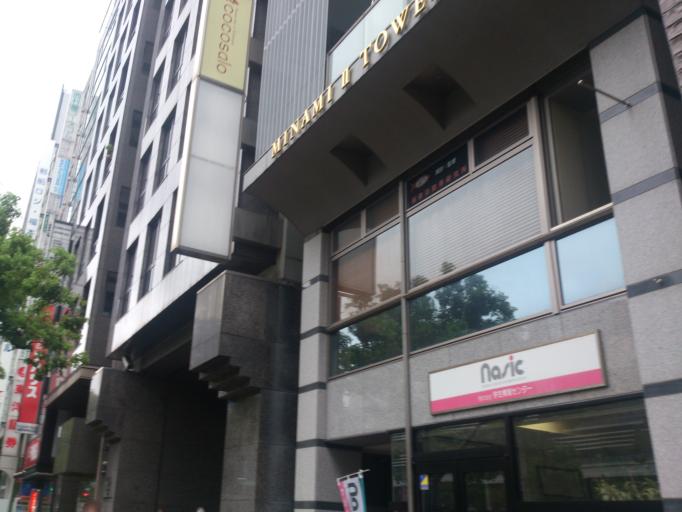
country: JP
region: Hyogo
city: Kobe
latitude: 34.6898
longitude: 135.1963
